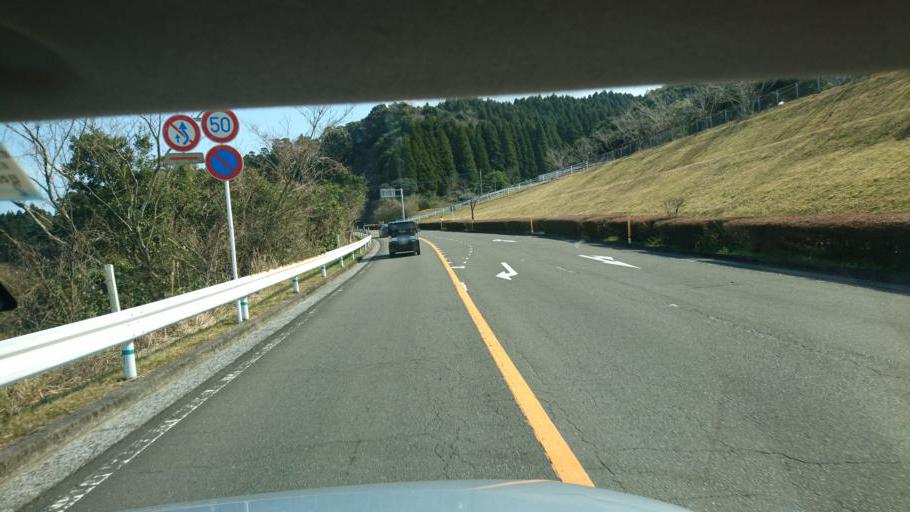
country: JP
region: Miyazaki
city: Miyazaki-shi
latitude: 31.8359
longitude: 131.4017
